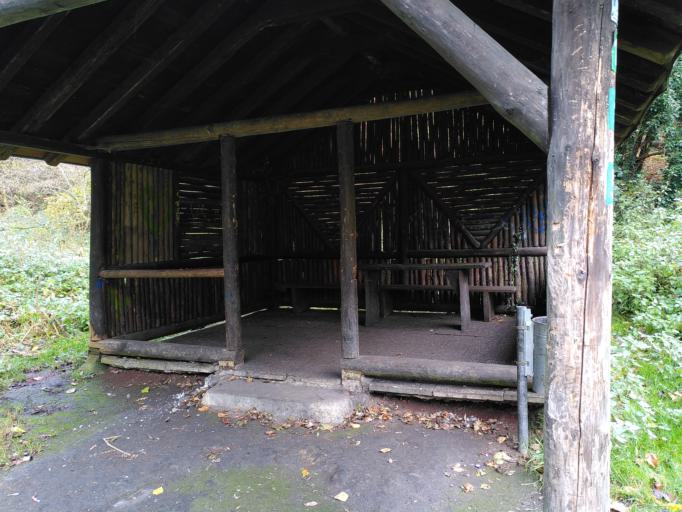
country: DE
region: Rheinland-Pfalz
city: Weitersburg
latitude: 50.4233
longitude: 7.5948
